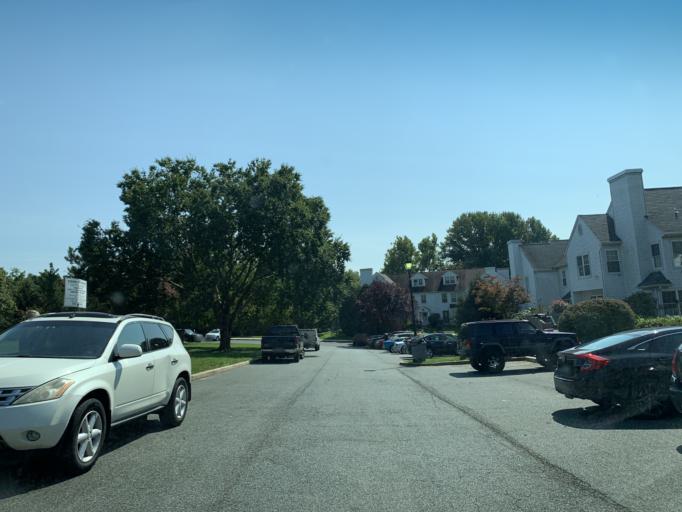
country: US
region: Maryland
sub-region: Harford County
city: Bel Air South
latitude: 39.4956
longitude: -76.3319
